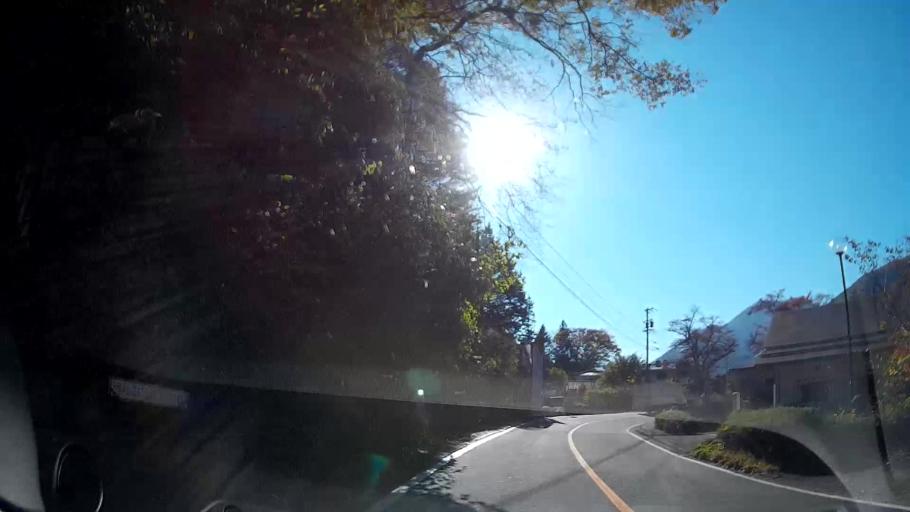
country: JP
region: Nagano
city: Toyoshina
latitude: 36.1630
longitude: 137.7639
